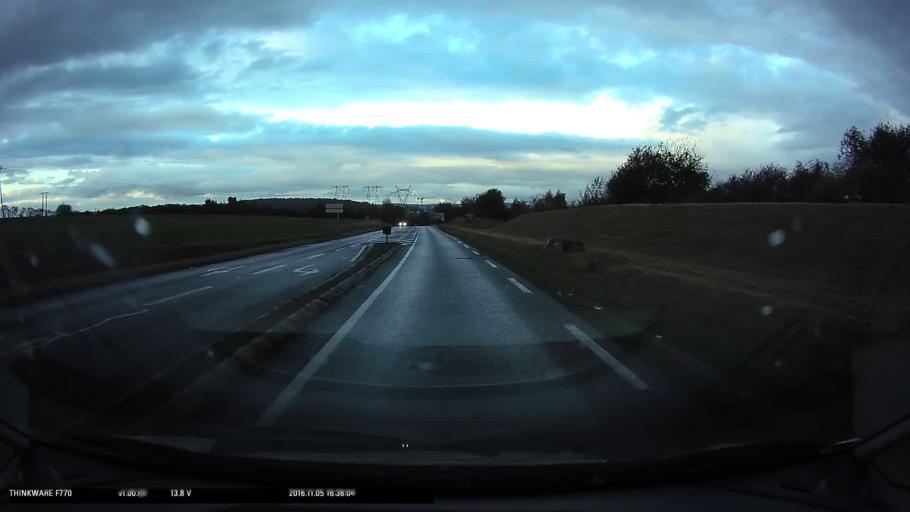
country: FR
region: Ile-de-France
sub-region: Departement du Val-d'Oise
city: Courdimanche
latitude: 49.0555
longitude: 2.0158
